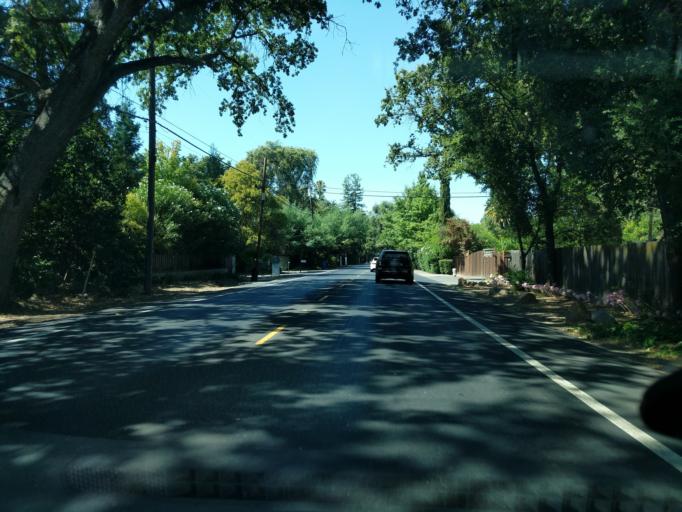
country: US
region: California
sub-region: Contra Costa County
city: Alamo
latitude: 37.8572
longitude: -122.0372
